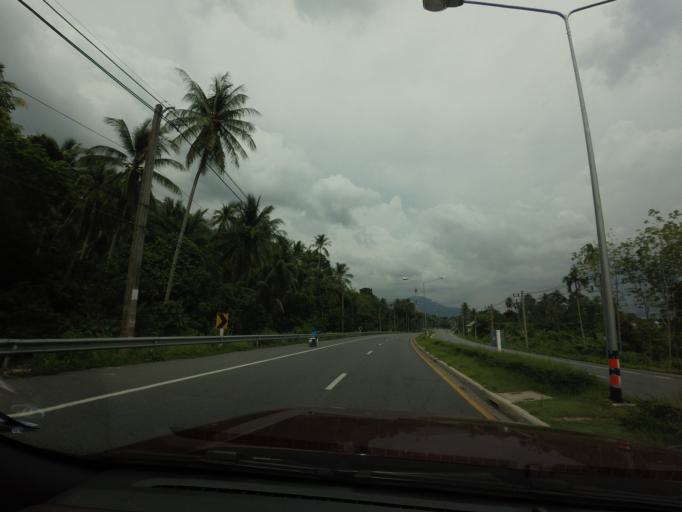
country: TH
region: Yala
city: Krong Pi Nang
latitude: 6.4691
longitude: 101.2694
